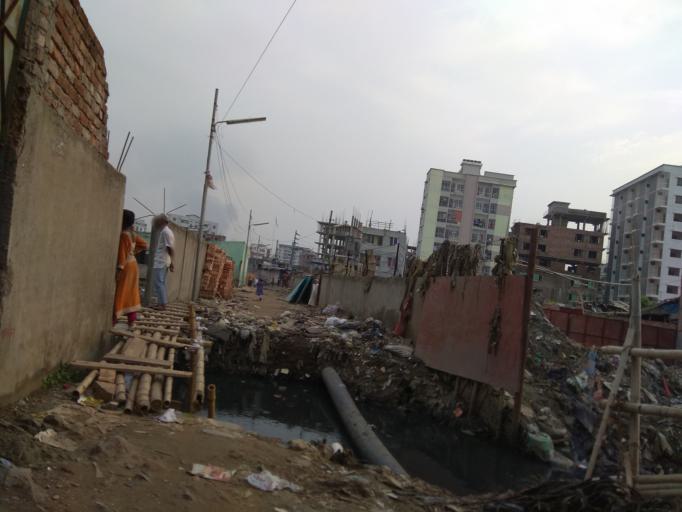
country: BD
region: Dhaka
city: Tungi
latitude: 23.8139
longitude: 90.3798
